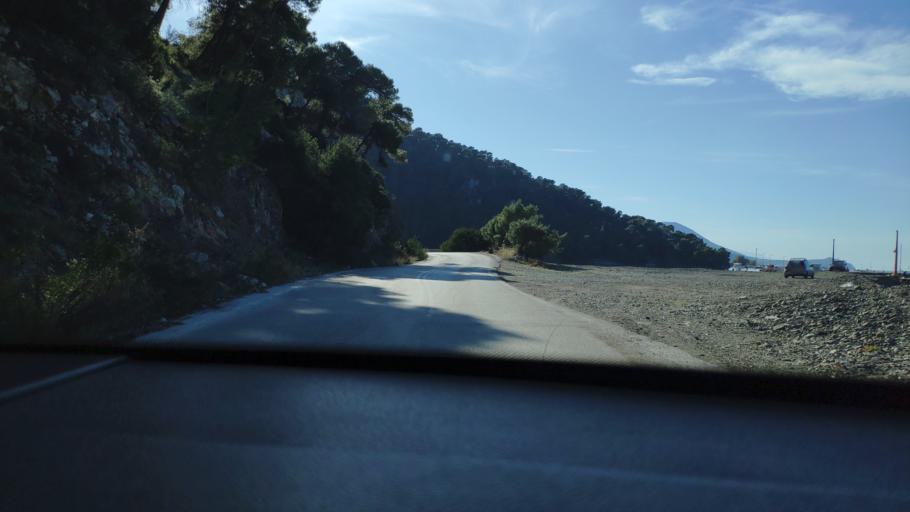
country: GR
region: Peloponnese
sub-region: Nomos Korinthias
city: Agioi Theodoroi
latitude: 38.0596
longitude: 23.1076
